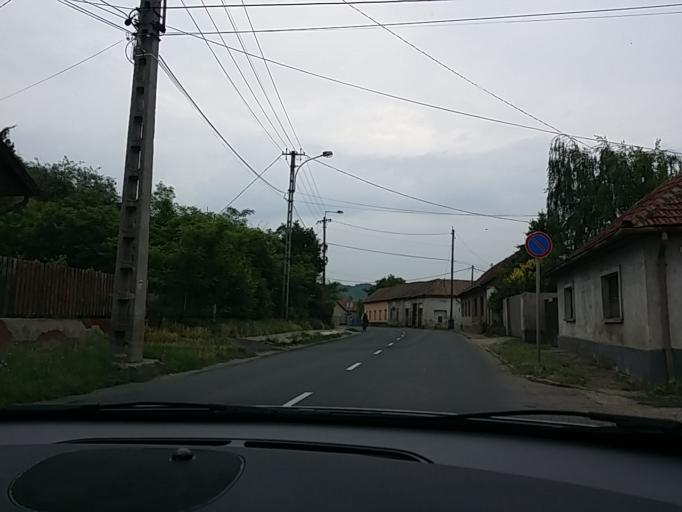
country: HU
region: Nograd
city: Batonyterenye
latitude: 48.0063
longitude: 19.8360
